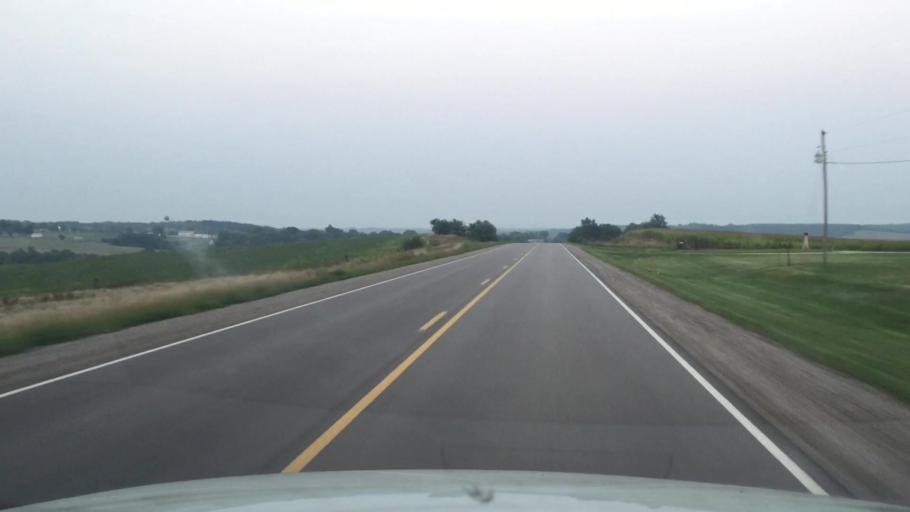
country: US
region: Iowa
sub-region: Marion County
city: Melcher-Dallas
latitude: 41.1894
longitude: -93.4006
